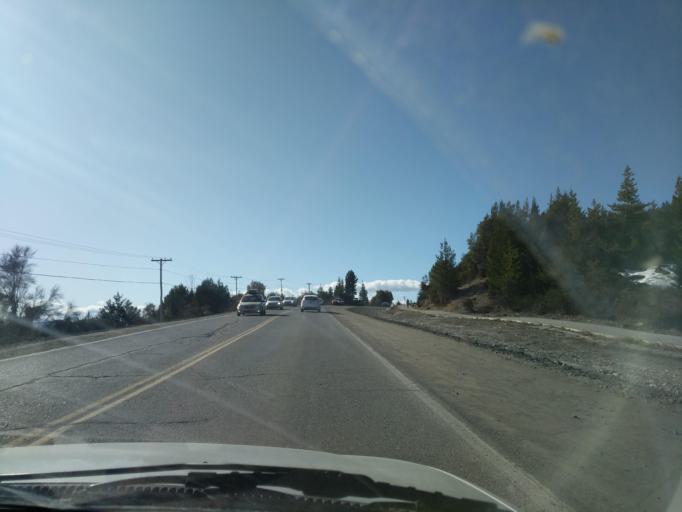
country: AR
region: Rio Negro
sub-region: Departamento de Bariloche
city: San Carlos de Bariloche
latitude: -41.1302
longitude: -71.4142
